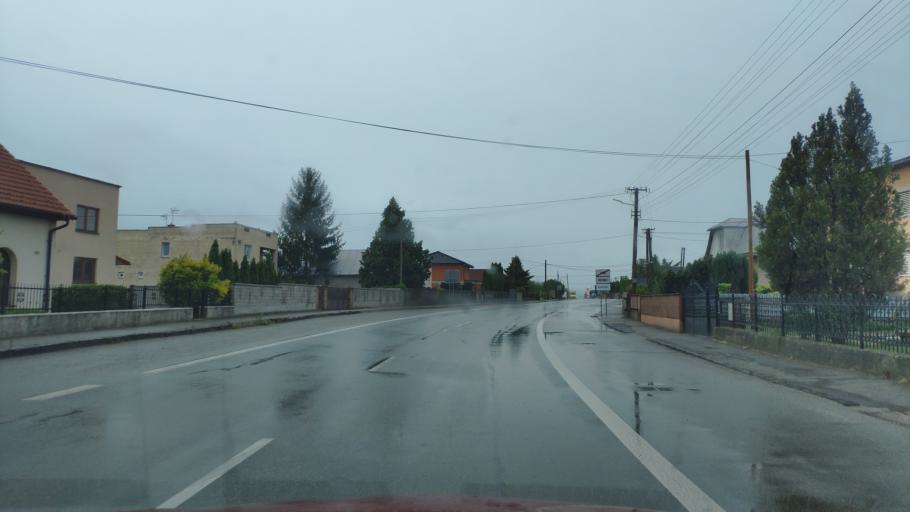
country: HU
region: Borsod-Abauj-Zemplen
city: Gonc
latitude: 48.5557
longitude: 21.2589
